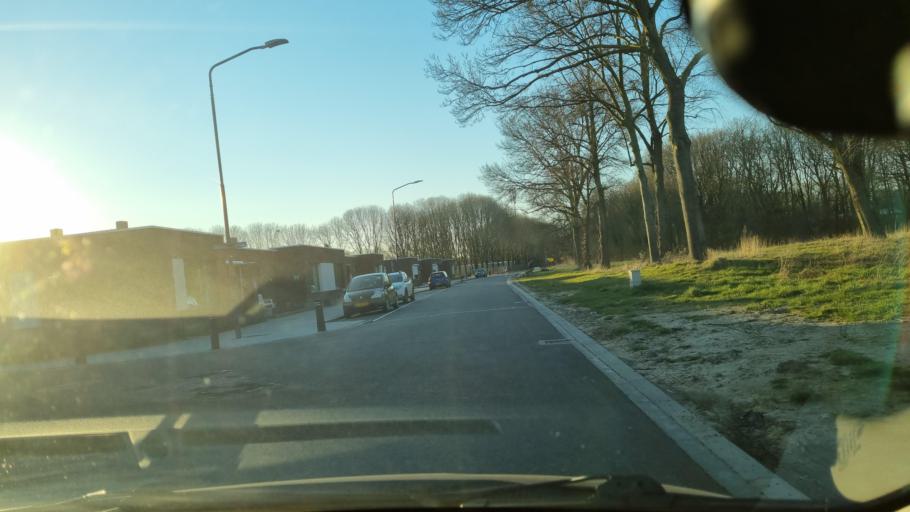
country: NL
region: Limburg
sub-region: Gemeente Sittard-Geleen
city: Sittard
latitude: 51.0060
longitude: 5.8907
